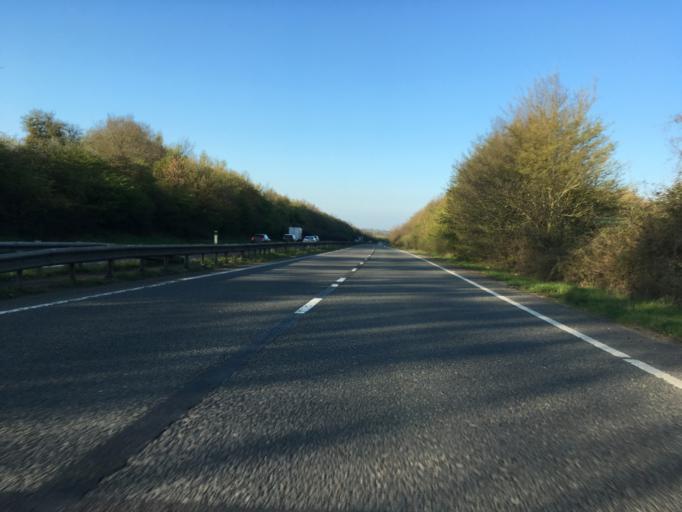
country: GB
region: England
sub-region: Oxfordshire
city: Witney
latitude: 51.7824
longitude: -1.4583
